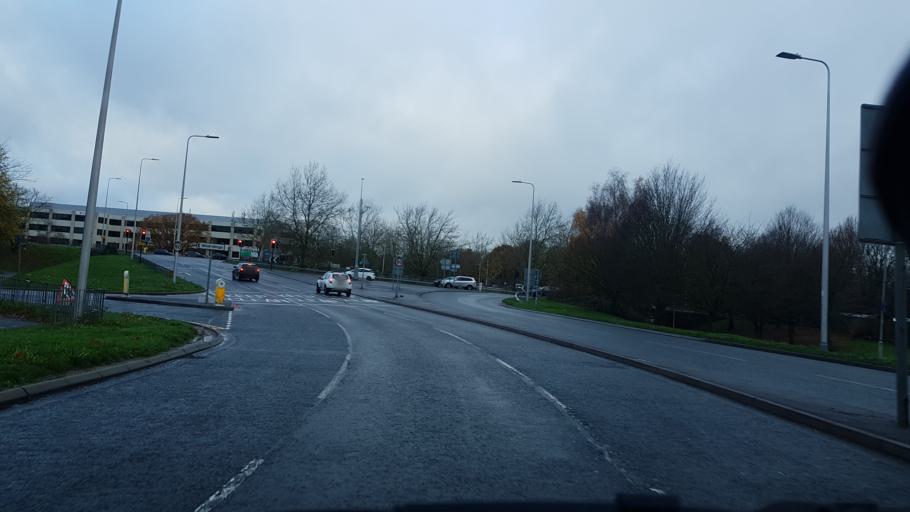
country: GB
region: England
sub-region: Bracknell Forest
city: Bracknell
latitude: 51.4125
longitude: -0.7589
